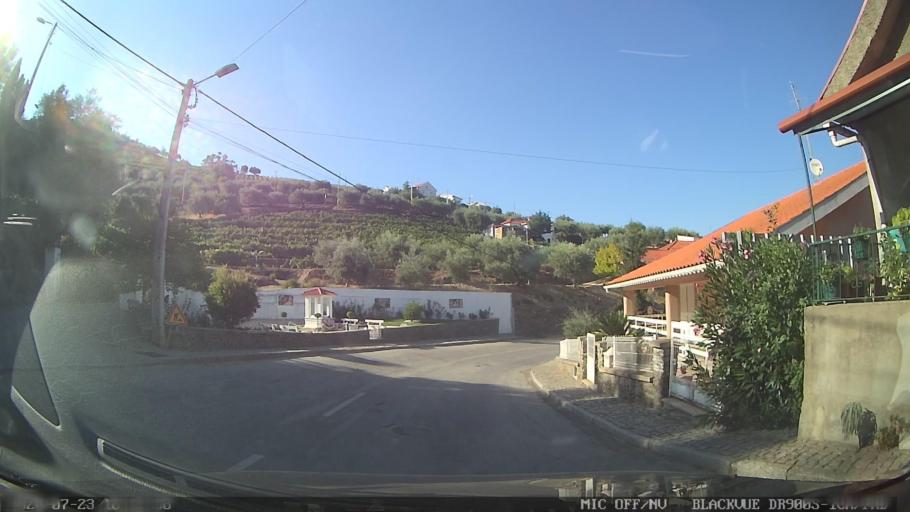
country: PT
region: Viseu
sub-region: Sao Joao da Pesqueira
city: Sao Joao da Pesqueira
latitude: 41.1818
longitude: -7.4176
